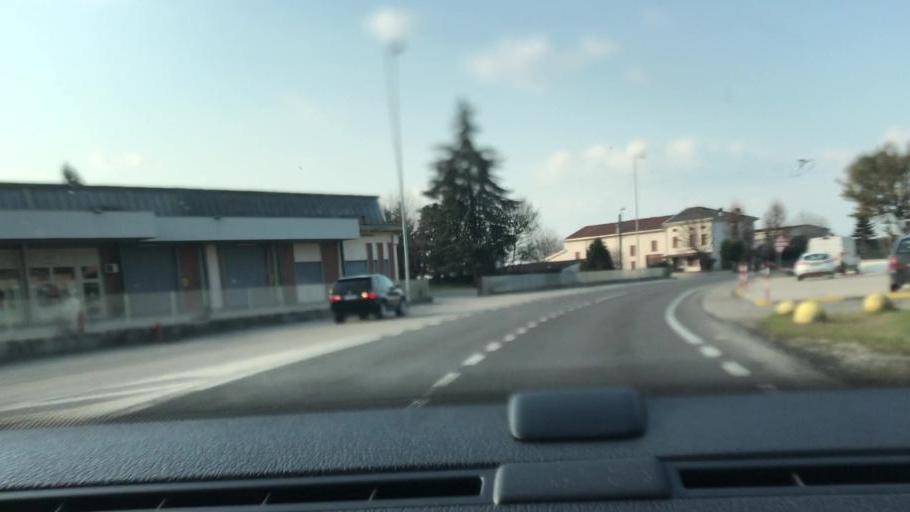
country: IT
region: Lombardy
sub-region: Provincia di Cremona
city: Vicomoscano
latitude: 44.9497
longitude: 10.4718
